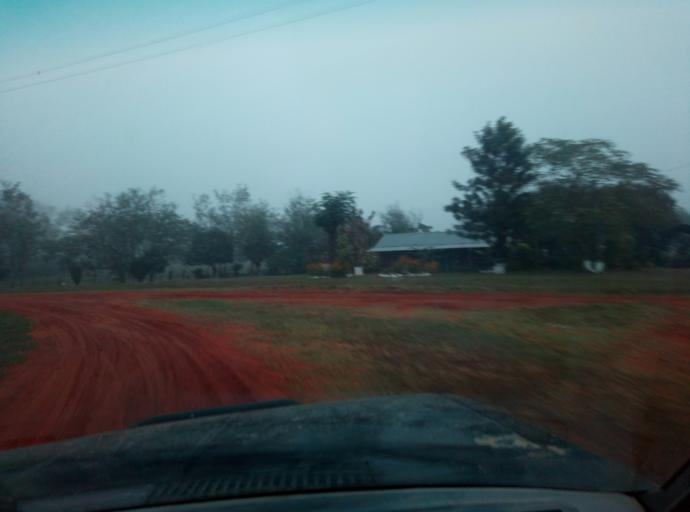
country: PY
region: Caaguazu
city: Doctor Cecilio Baez
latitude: -25.1545
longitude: -56.2912
